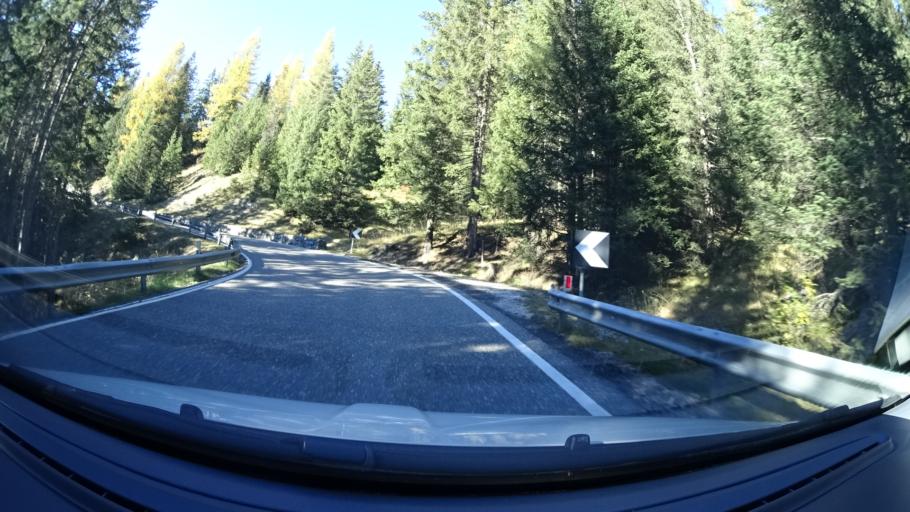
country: IT
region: Trentino-Alto Adige
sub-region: Provincia di Trento
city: Canazei
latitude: 46.4895
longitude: 11.7837
